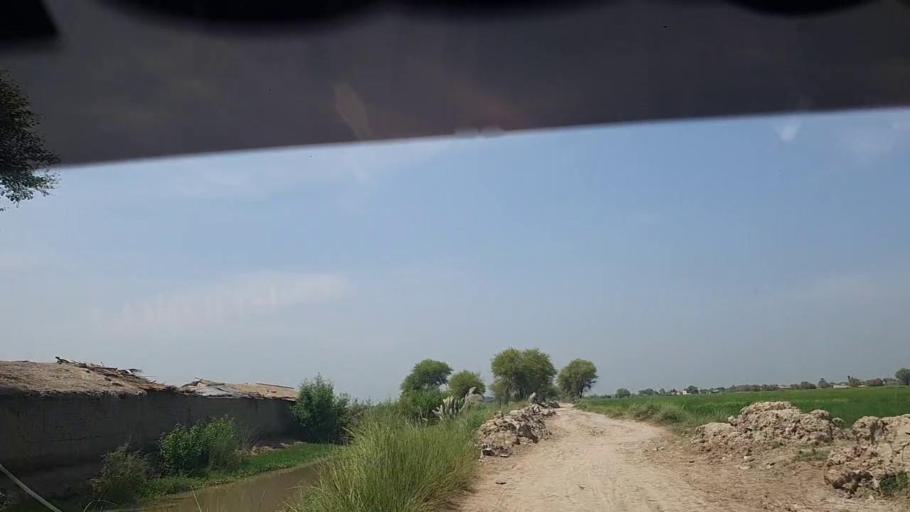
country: PK
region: Sindh
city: Thul
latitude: 28.1845
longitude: 68.7215
